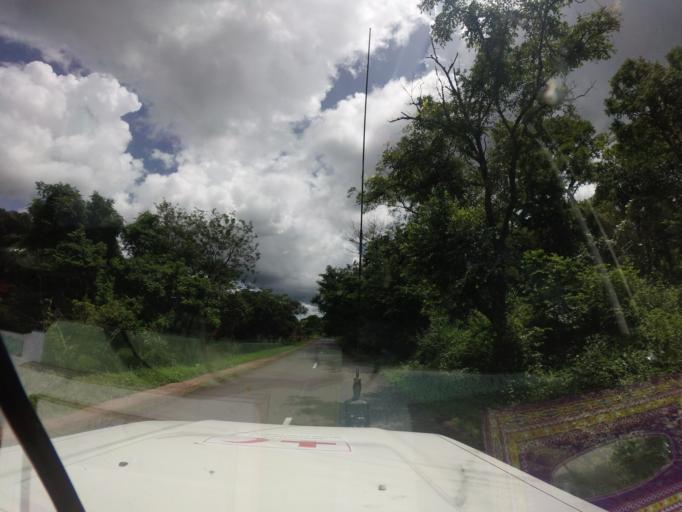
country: SL
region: Northern Province
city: Bindi
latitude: 10.1543
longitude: -11.5358
